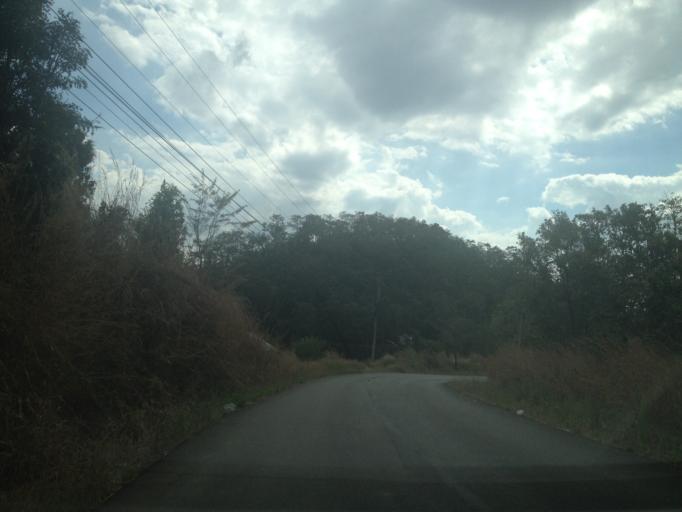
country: TH
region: Mae Hong Son
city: Ban Huai I Huak
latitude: 18.1459
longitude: 98.2185
